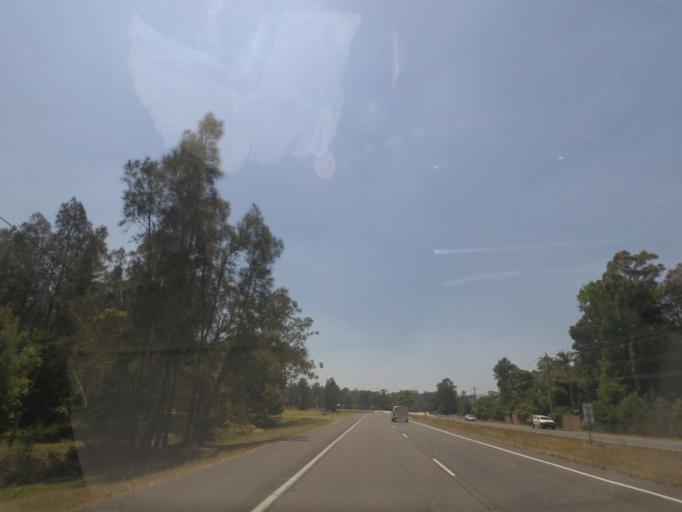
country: AU
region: New South Wales
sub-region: Port Stephens Shire
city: Medowie
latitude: -32.7905
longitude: 151.9009
